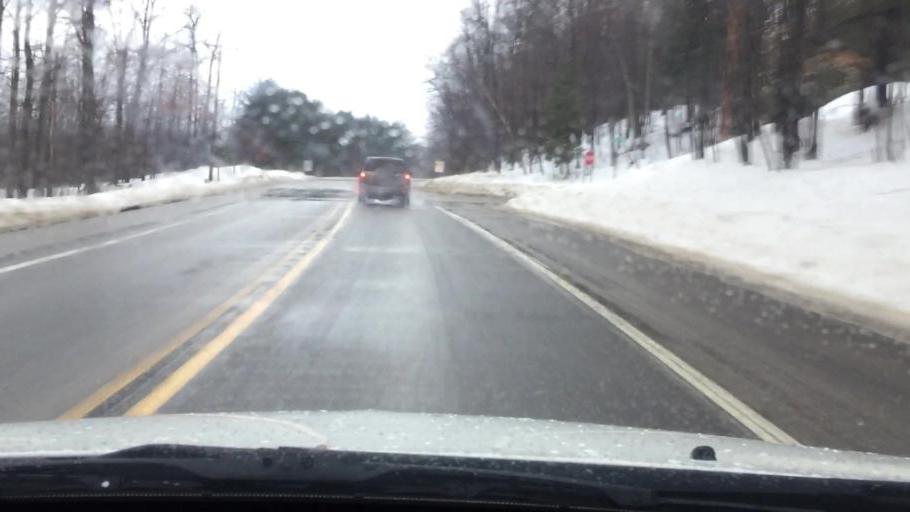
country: US
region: Michigan
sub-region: Charlevoix County
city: East Jordan
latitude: 45.2202
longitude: -85.1745
